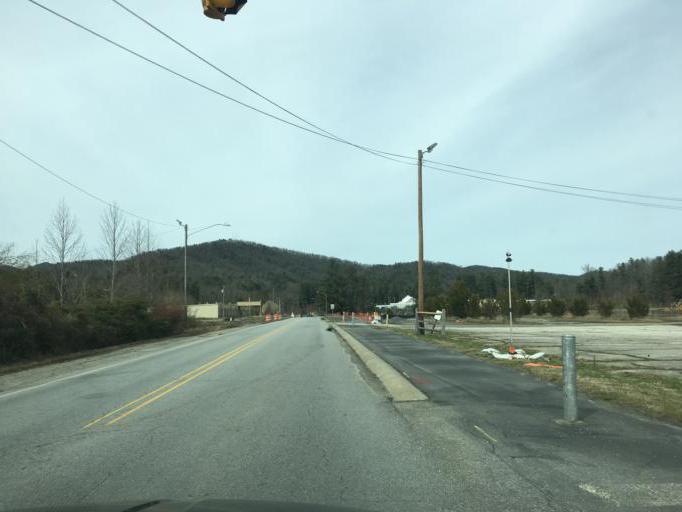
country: US
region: North Carolina
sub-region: Transylvania County
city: Brevard
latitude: 35.2667
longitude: -82.7059
